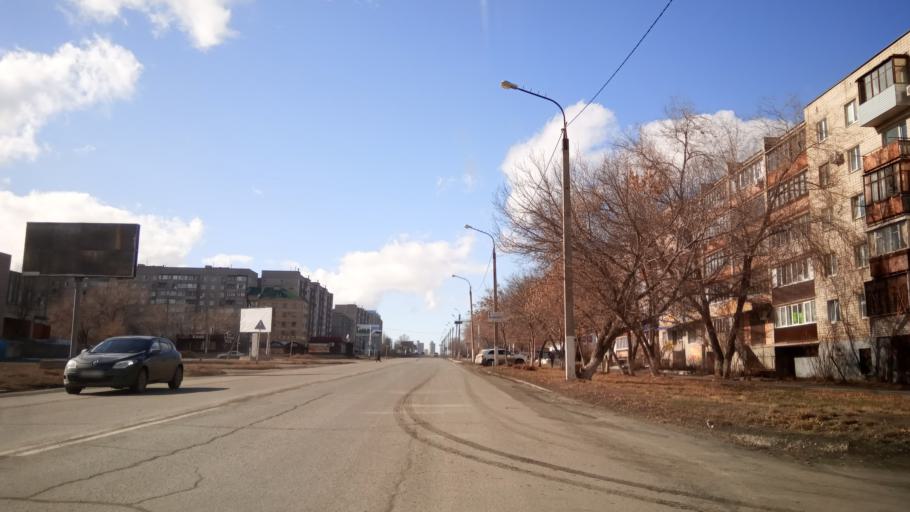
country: RU
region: Orenburg
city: Novotroitsk
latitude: 51.1849
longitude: 58.2795
